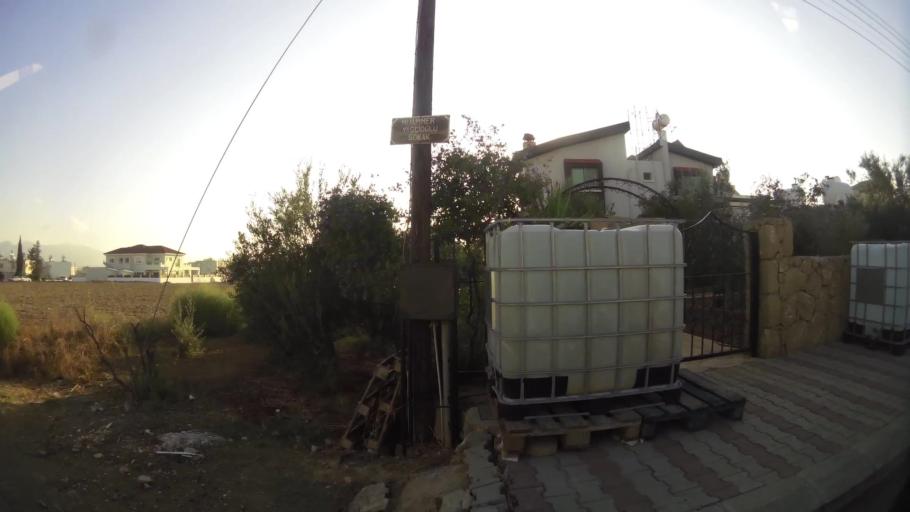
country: CY
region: Lefkosia
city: Nicosia
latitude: 35.1959
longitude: 33.3261
